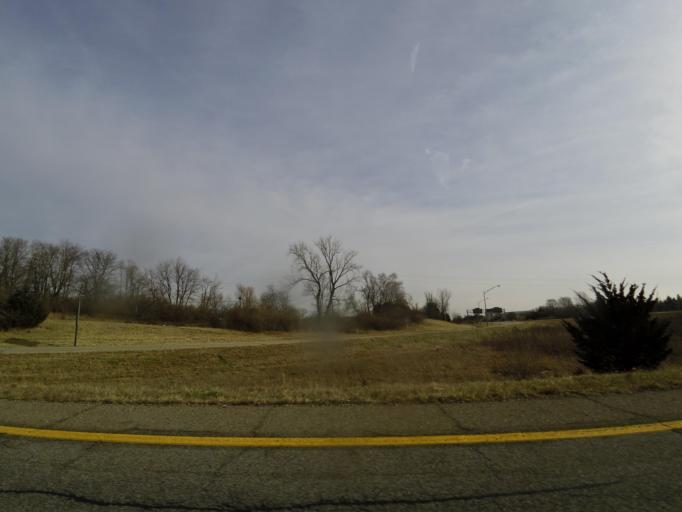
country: US
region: Illinois
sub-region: McLean County
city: Bloomington
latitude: 40.4370
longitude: -88.9891
